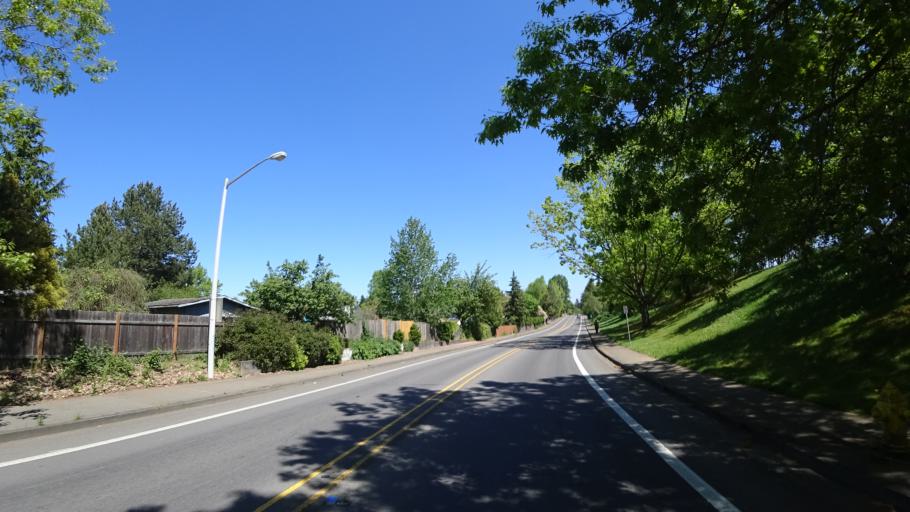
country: US
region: Oregon
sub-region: Washington County
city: Hillsboro
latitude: 45.5089
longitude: -122.9587
